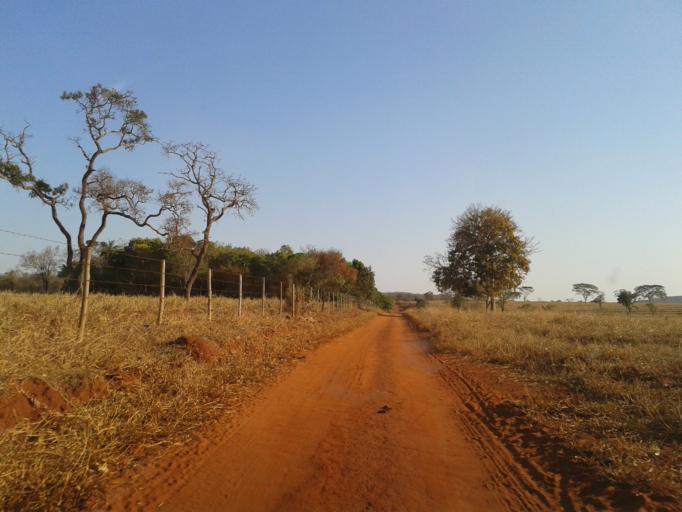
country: BR
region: Minas Gerais
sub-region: Campina Verde
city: Campina Verde
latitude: -19.2501
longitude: -49.6099
